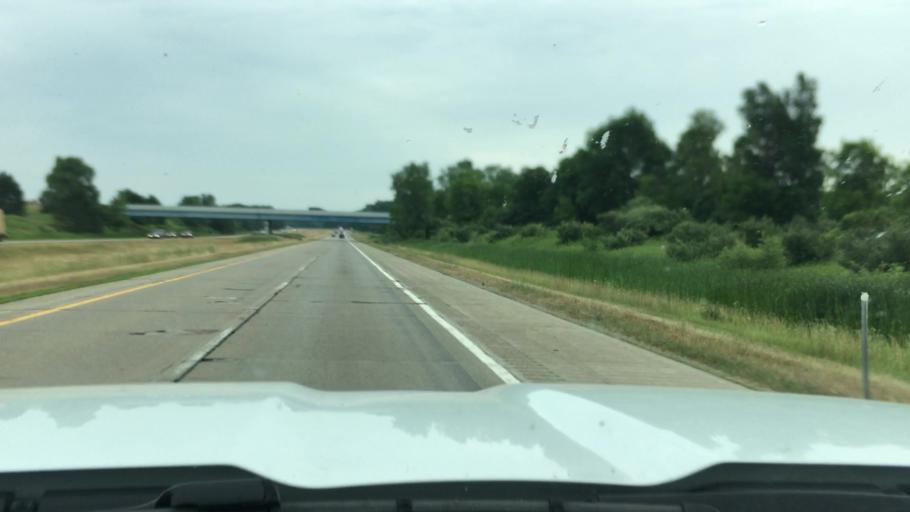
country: US
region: Michigan
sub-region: Clinton County
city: DeWitt
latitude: 42.8074
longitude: -84.6058
